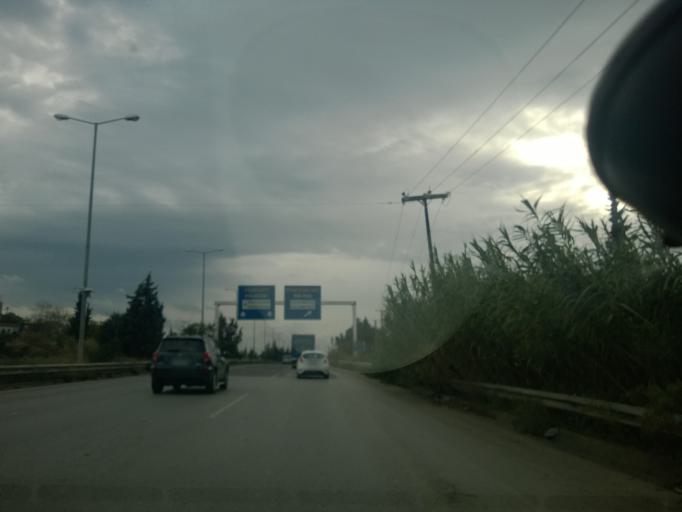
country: GR
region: Central Macedonia
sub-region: Nomos Thessalonikis
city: Pylaia
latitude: 40.5863
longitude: 22.9718
